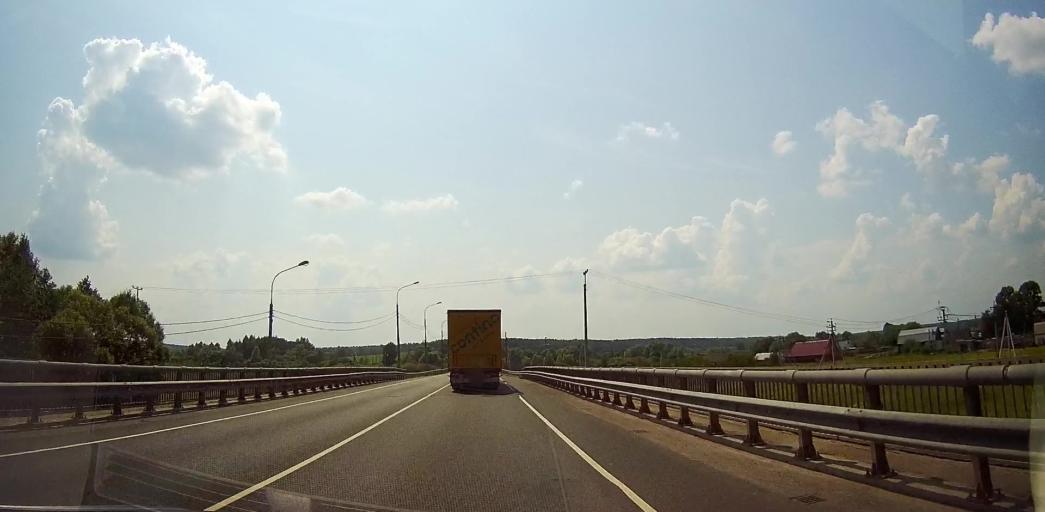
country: RU
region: Moskovskaya
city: Meshcherino
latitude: 55.1899
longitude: 38.3605
